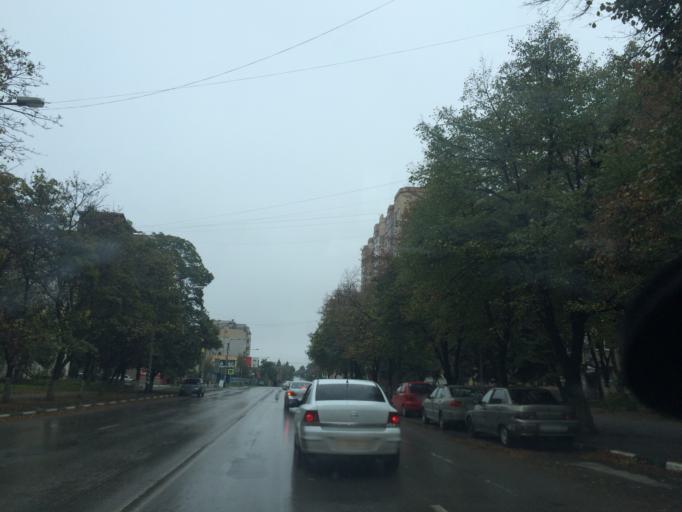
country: RU
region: Rostov
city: Azov
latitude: 47.1082
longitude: 39.4289
